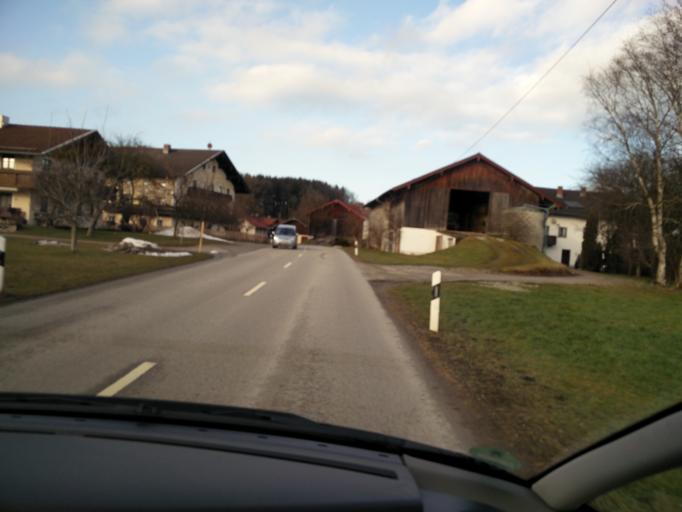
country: DE
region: Bavaria
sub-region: Upper Bavaria
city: Hoslwang
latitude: 47.9436
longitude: 12.3409
